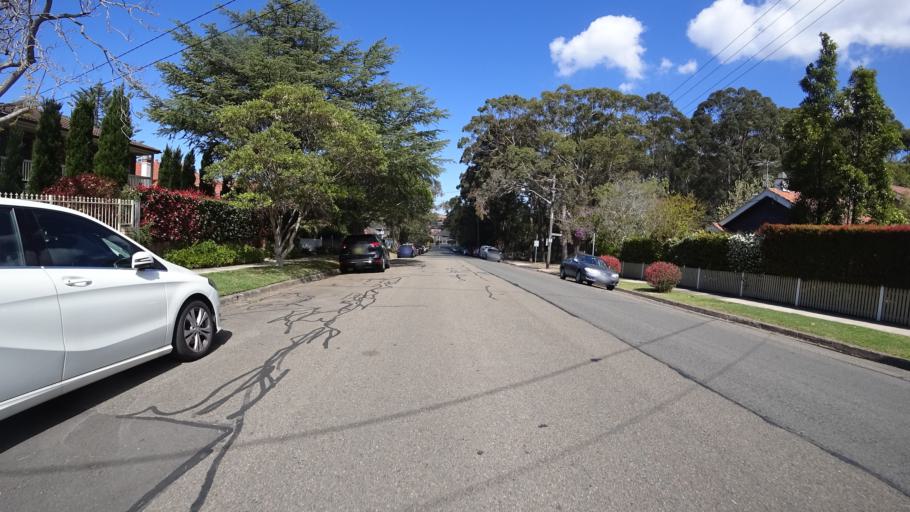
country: AU
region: New South Wales
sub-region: Willoughby
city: Chatswood
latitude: -33.7894
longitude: 151.1877
